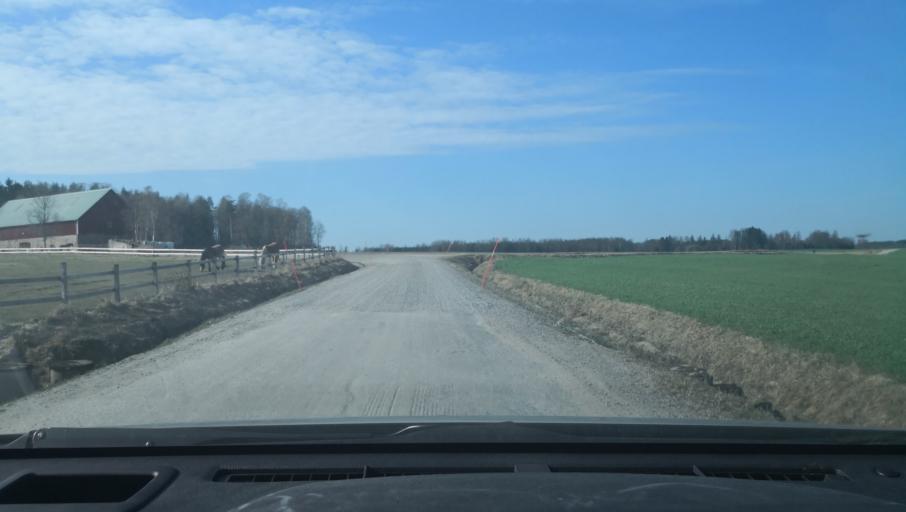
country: SE
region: Uppsala
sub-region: Heby Kommun
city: Morgongava
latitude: 59.8448
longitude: 16.9137
